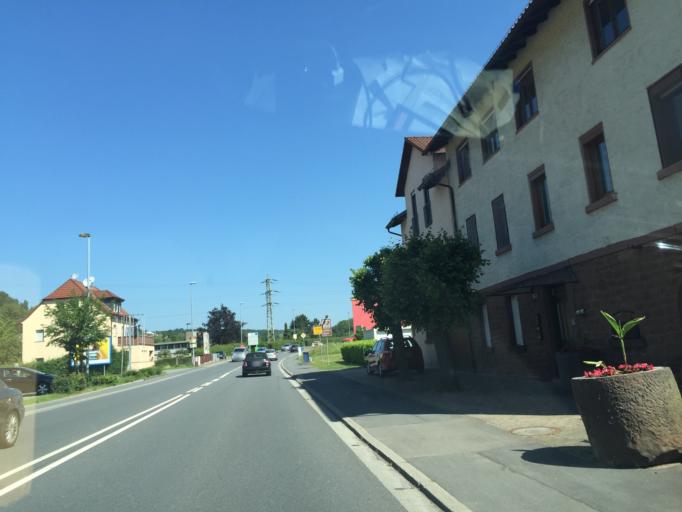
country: DE
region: Hesse
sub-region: Regierungsbezirk Darmstadt
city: Erbach
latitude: 49.6488
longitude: 8.9939
